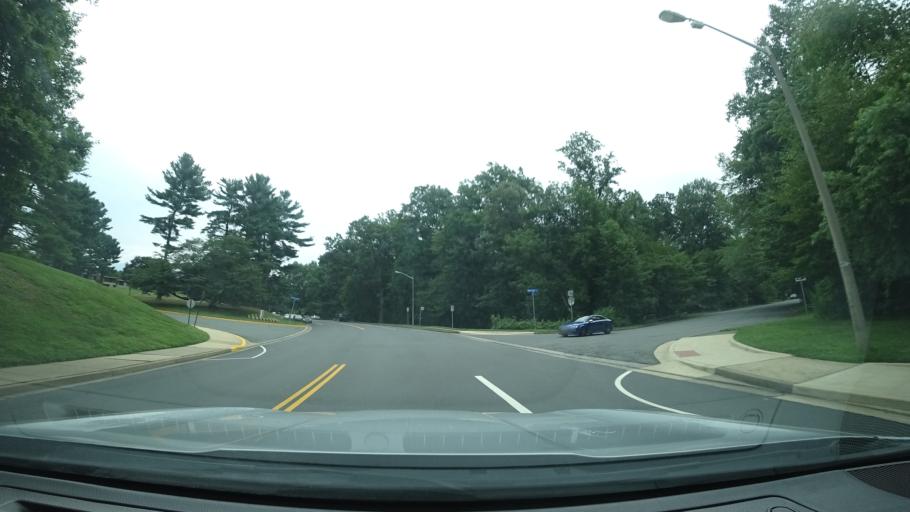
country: US
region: Virginia
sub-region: Fairfax County
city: Reston
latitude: 38.9694
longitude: -77.3392
